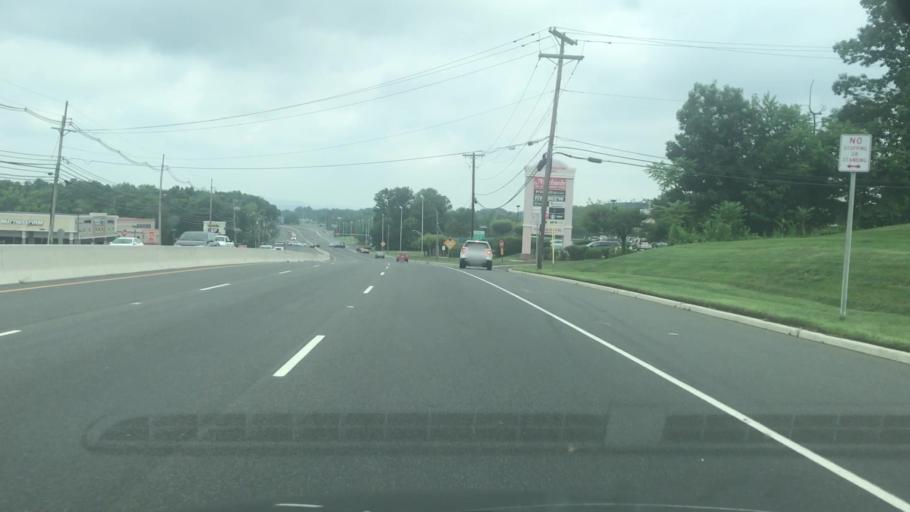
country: US
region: New Jersey
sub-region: Passaic County
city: Wayne
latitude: 40.9382
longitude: -74.2696
